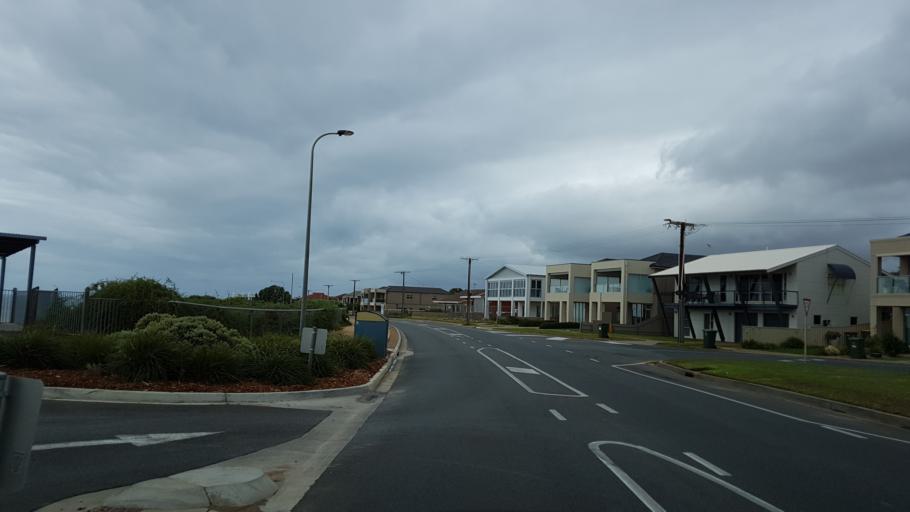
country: AU
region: South Australia
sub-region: Onkaparinga
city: Port Willunga
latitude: -35.2815
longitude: 138.4439
